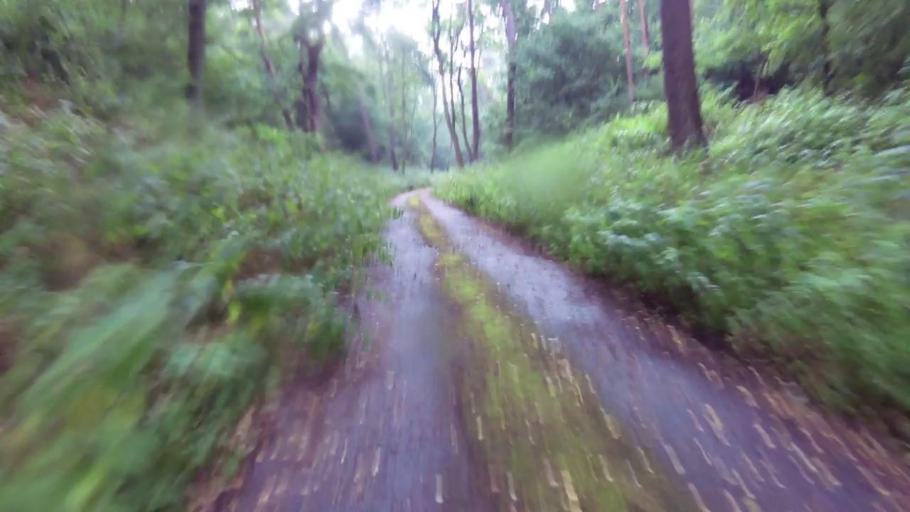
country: PL
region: West Pomeranian Voivodeship
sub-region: Powiat choszczenski
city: Recz
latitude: 53.2435
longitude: 15.4633
